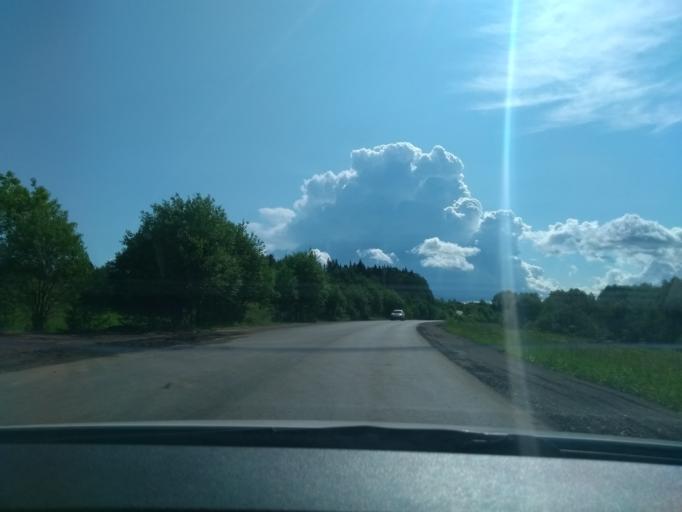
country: RU
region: Perm
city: Kukushtan
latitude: 57.8168
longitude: 56.5401
